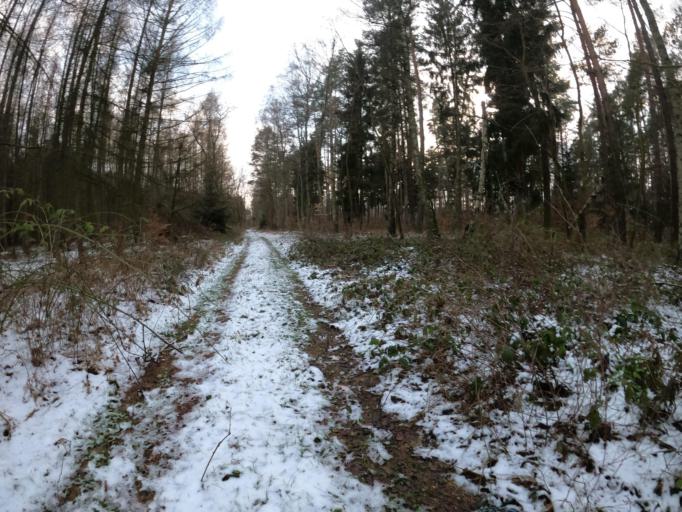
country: PL
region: Lubusz
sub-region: Powiat slubicki
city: Cybinka
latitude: 52.1881
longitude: 14.8729
